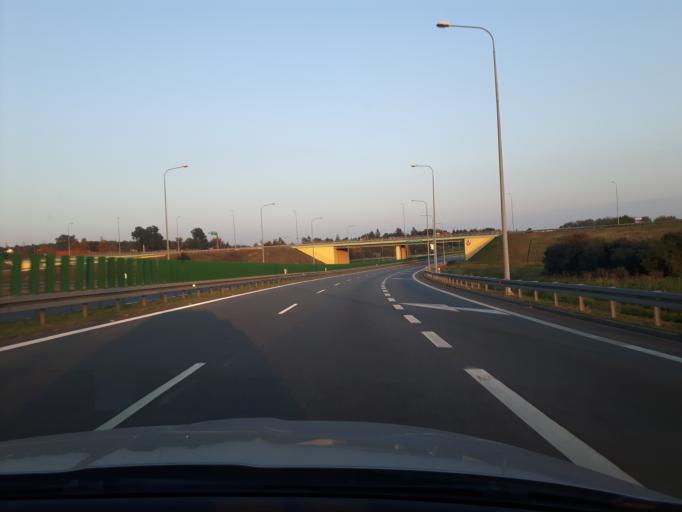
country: PL
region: Warmian-Masurian Voivodeship
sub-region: Powiat elblaski
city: Gronowo Gorne
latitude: 54.1377
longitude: 19.4476
